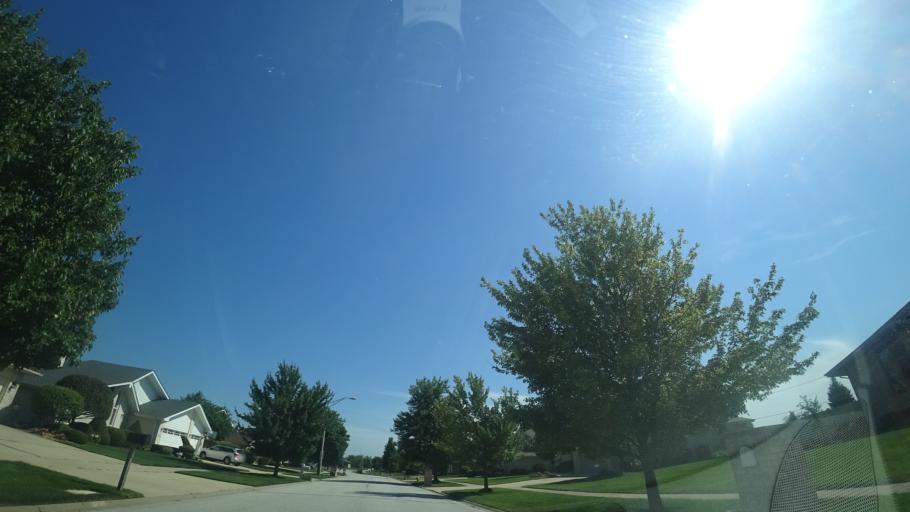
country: US
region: Illinois
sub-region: Will County
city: Homer Glen
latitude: 41.5689
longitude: -87.9087
